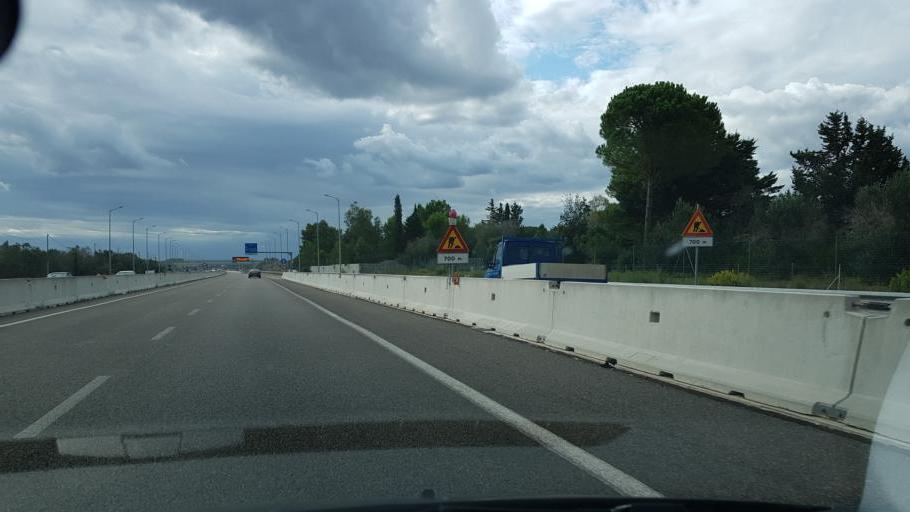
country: IT
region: Apulia
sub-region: Provincia di Lecce
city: Muro Leccese
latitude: 40.1258
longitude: 18.3448
